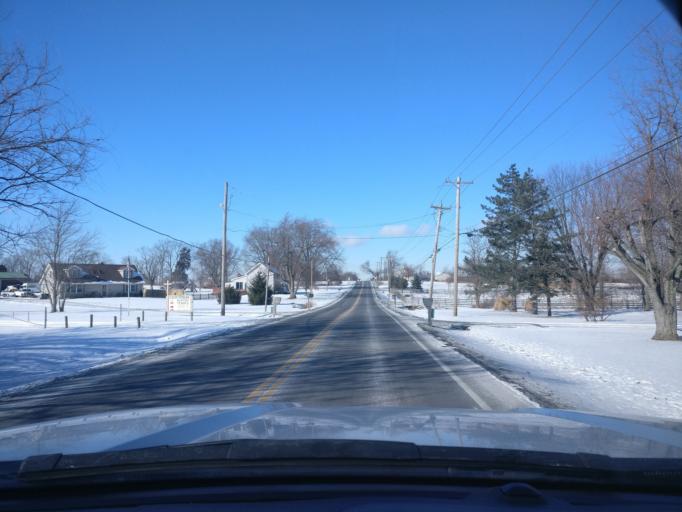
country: US
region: Ohio
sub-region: Warren County
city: Hunter
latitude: 39.4982
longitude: -84.2576
